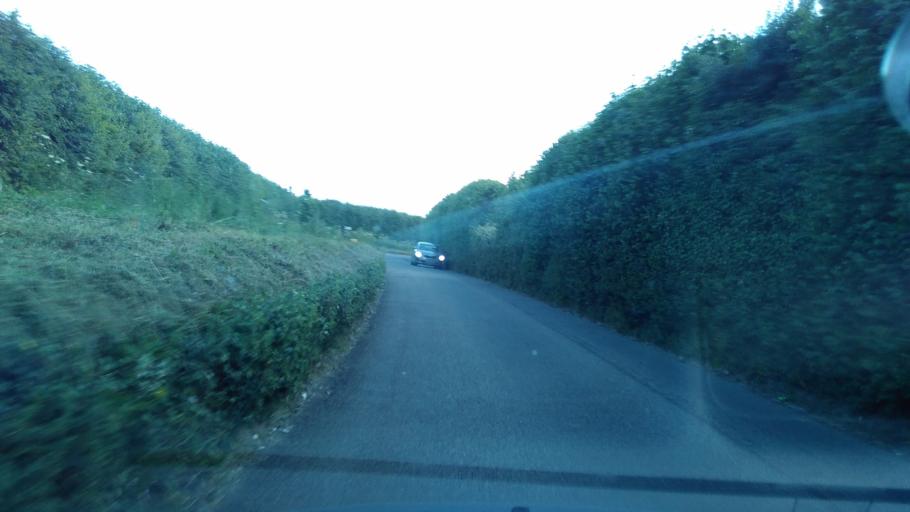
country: GB
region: England
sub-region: Kent
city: Dunkirk
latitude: 51.2735
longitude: 0.9400
